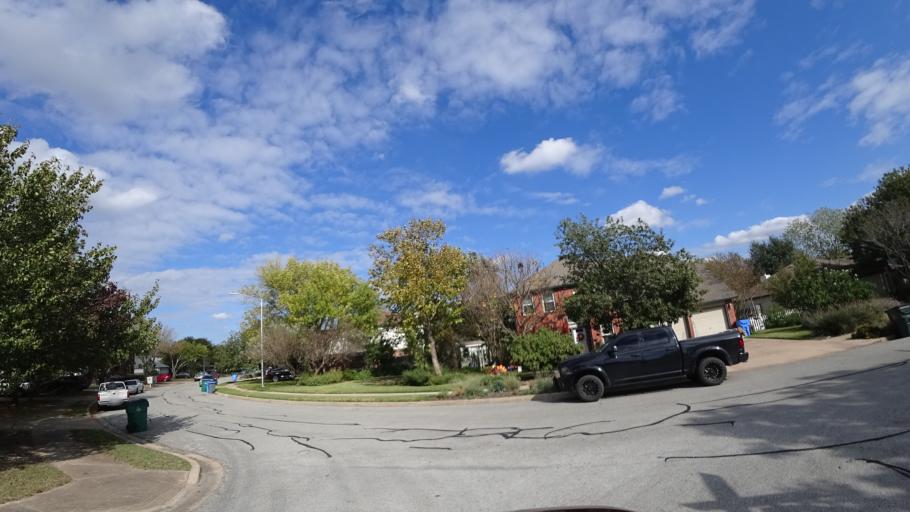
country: US
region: Texas
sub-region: Travis County
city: Pflugerville
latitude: 30.4361
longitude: -97.6364
